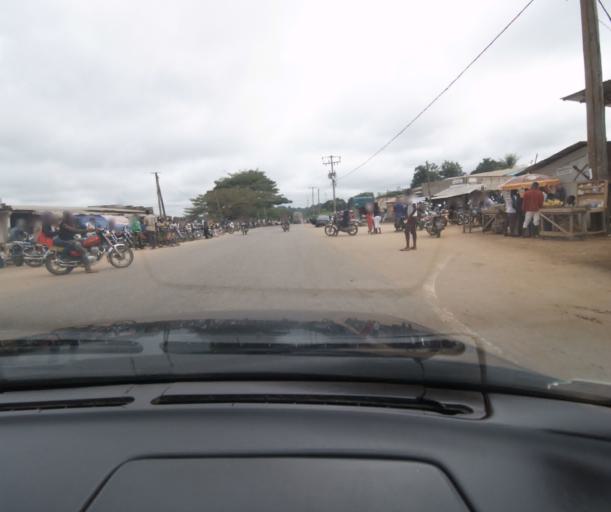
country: CM
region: Centre
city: Ombesa
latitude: 4.6029
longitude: 11.2566
